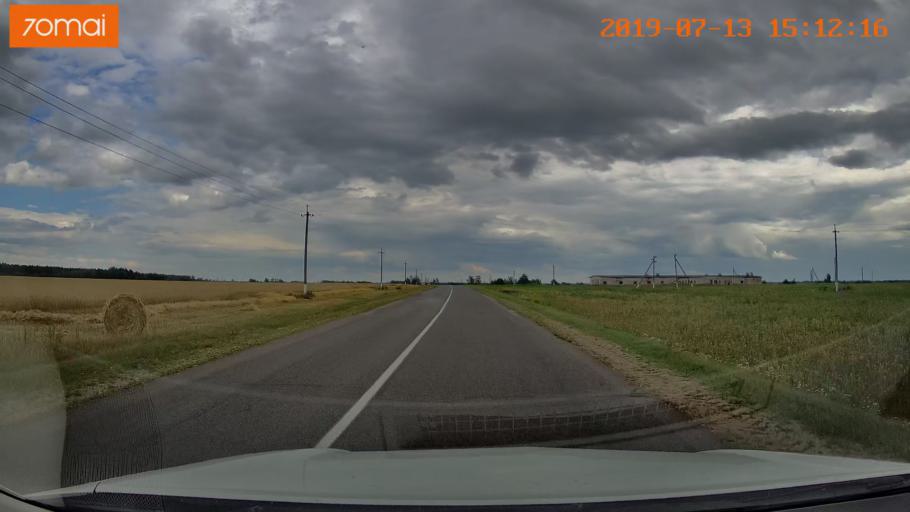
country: BY
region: Mogilev
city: Hlusha
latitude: 53.1513
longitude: 28.7887
